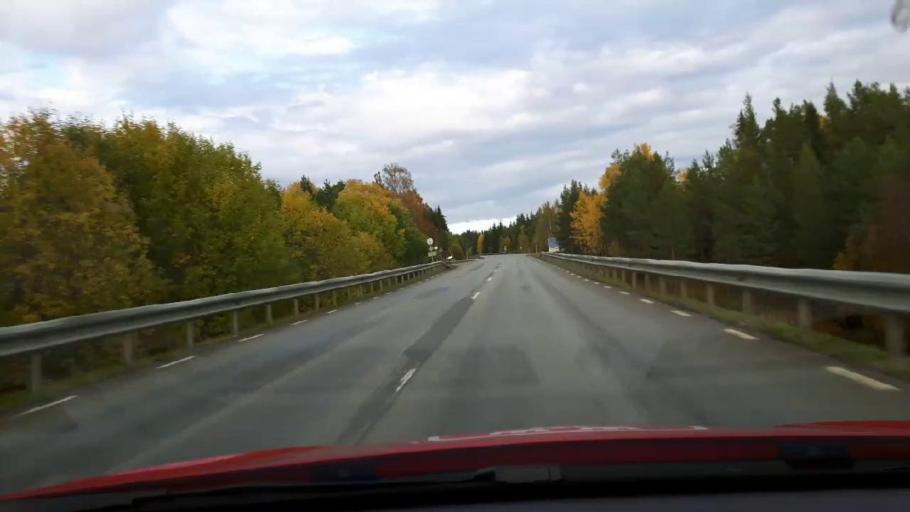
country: SE
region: Jaemtland
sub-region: Krokoms Kommun
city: Krokom
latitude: 63.3572
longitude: 14.4922
